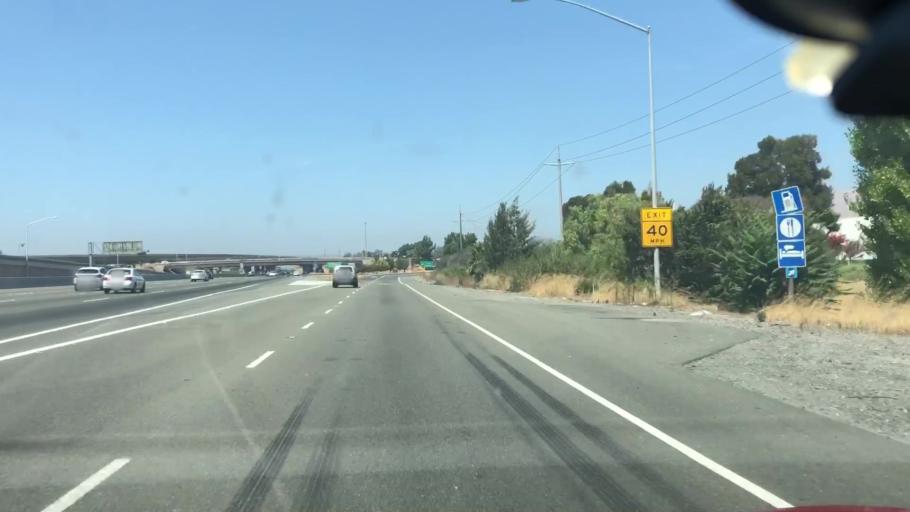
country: US
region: California
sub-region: Santa Clara County
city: Milpitas
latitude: 37.4224
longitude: -121.9142
